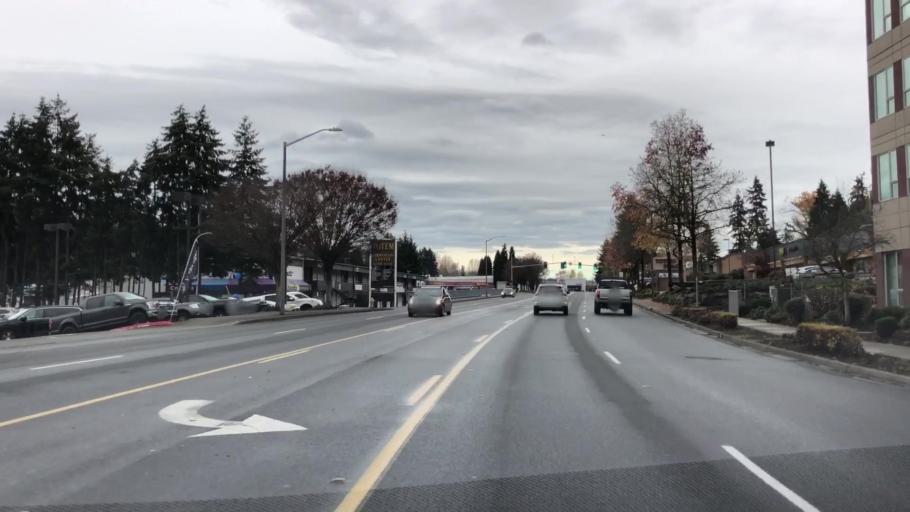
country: US
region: Washington
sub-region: King County
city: Kingsgate
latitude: 47.7100
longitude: -122.1721
